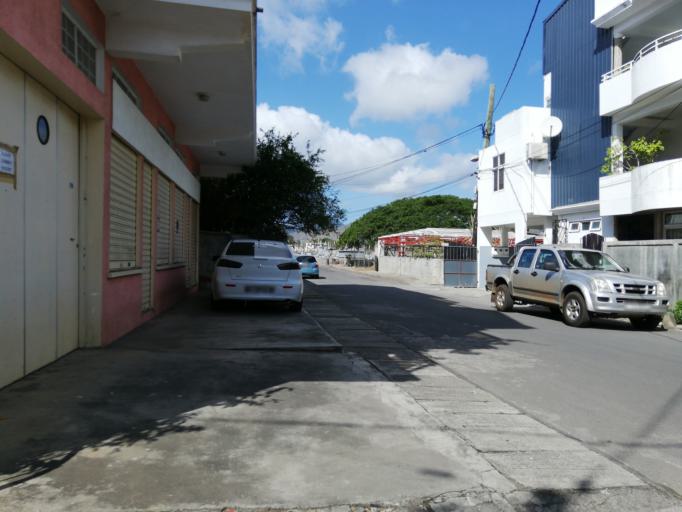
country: MU
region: Port Louis
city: Port Louis
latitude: -20.1616
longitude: 57.4837
